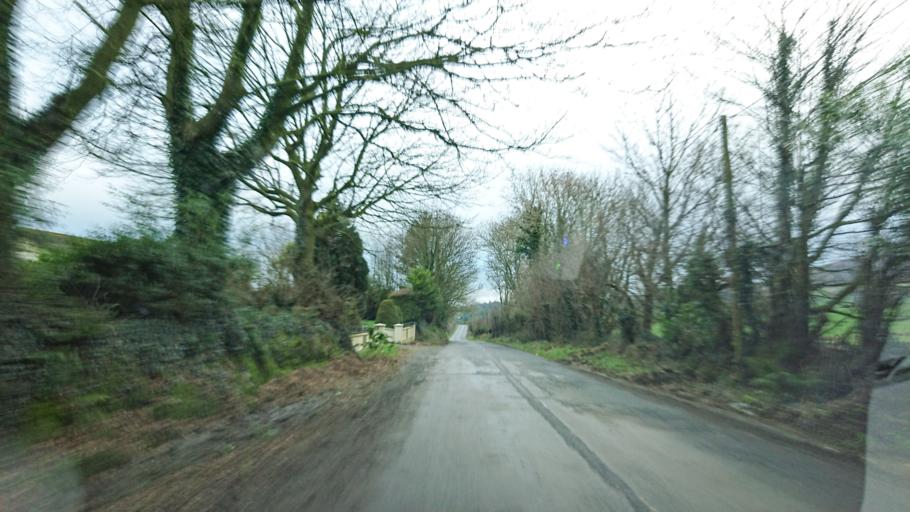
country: IE
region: Munster
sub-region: Waterford
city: Portlaw
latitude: 52.2519
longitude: -7.4098
